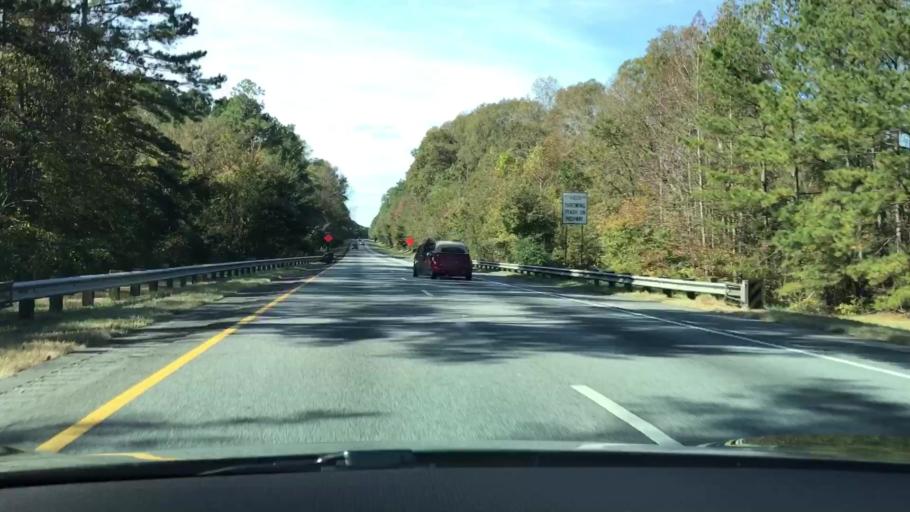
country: US
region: Georgia
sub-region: Morgan County
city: Madison
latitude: 33.5774
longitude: -83.5504
